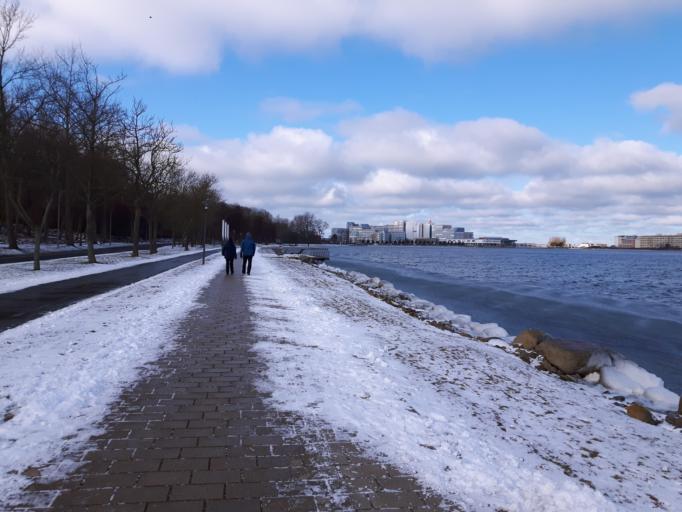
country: DE
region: Schleswig-Holstein
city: Heiligenhafen
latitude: 54.3749
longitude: 10.9647
